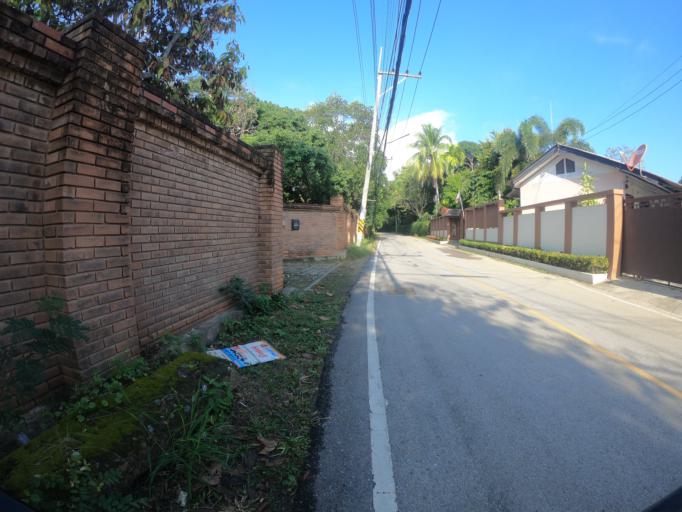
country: TH
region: Chiang Mai
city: Chiang Mai
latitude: 18.8178
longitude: 98.9539
